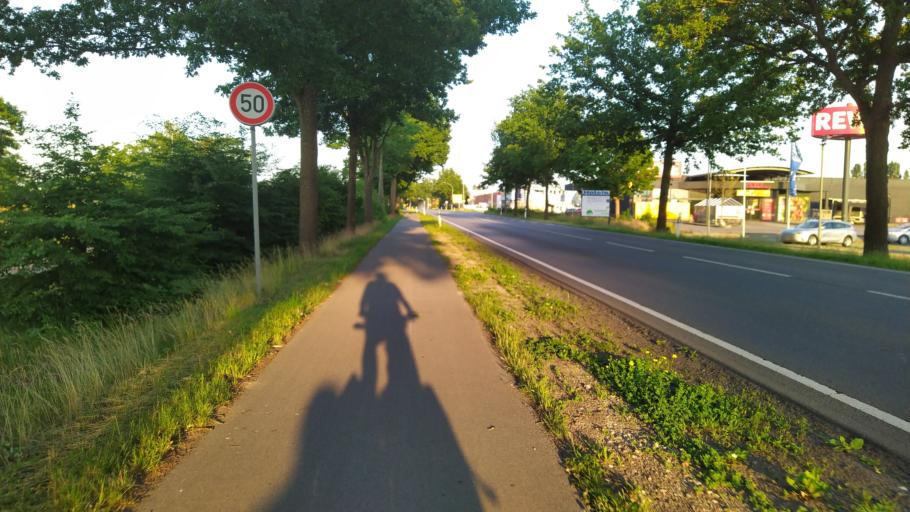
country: DE
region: Lower Saxony
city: Bei der Hohne
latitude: 53.4945
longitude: 9.1169
